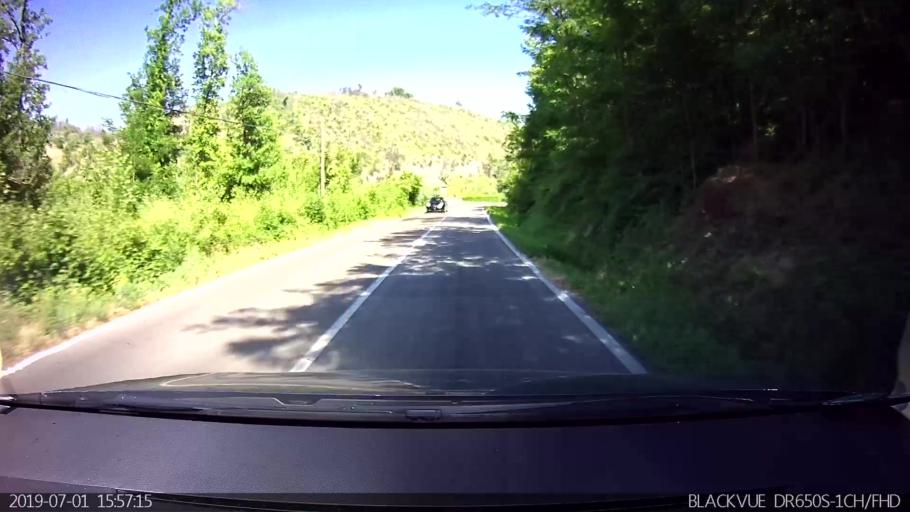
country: IT
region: Latium
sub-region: Provincia di Frosinone
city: Veroli
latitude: 41.6773
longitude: 13.4200
